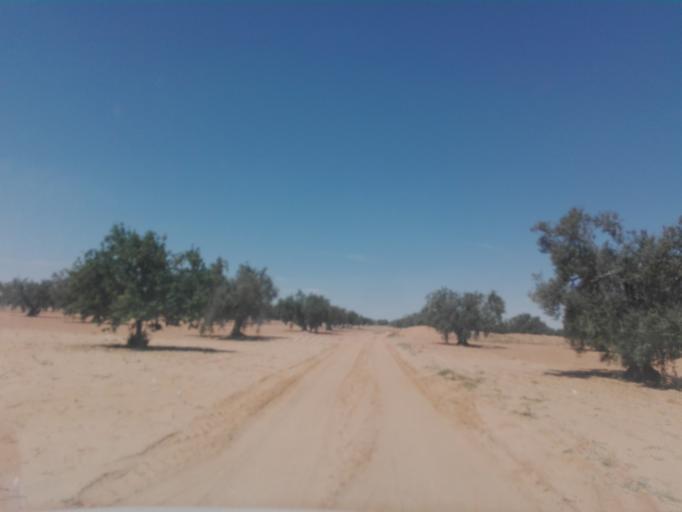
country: TN
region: Safaqis
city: Bi'r `Ali Bin Khalifah
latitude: 34.6627
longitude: 10.3135
